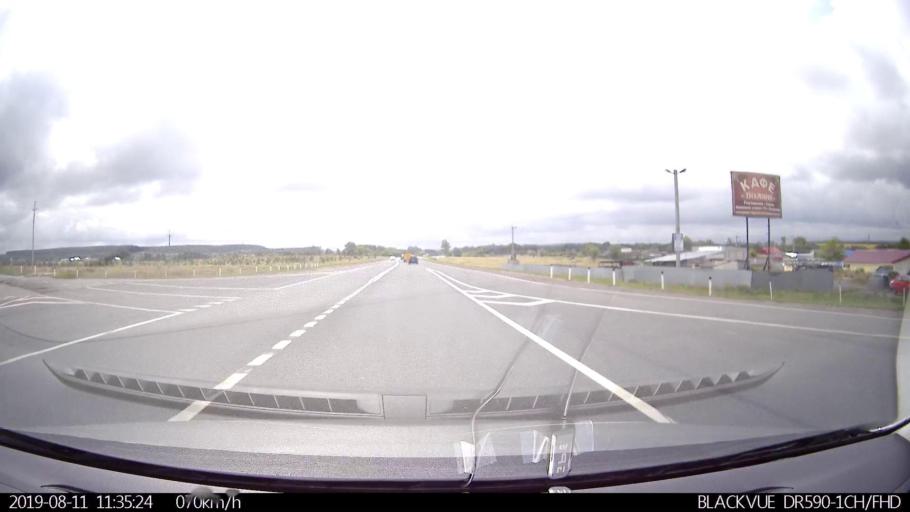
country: RU
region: Ulyanovsk
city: Silikatnyy
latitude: 54.0068
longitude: 48.2193
